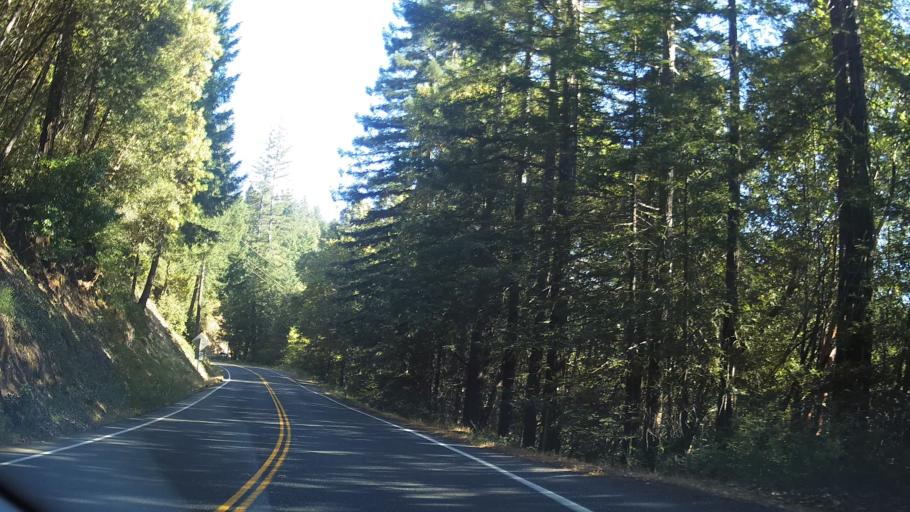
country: US
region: California
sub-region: Mendocino County
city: Brooktrails
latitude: 39.3907
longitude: -123.4678
